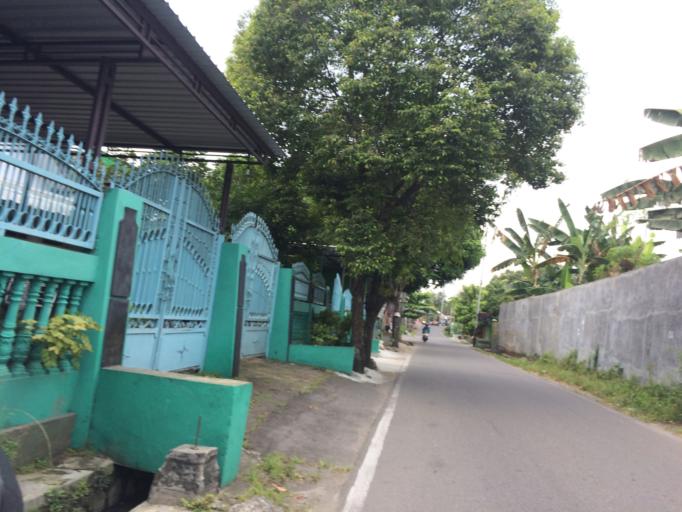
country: ID
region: Central Java
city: Grogol
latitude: -7.5930
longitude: 110.8210
